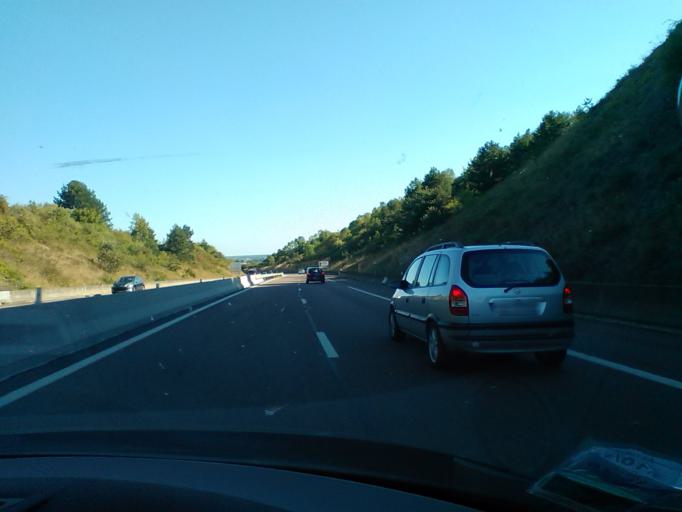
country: FR
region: Bourgogne
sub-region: Departement de la Cote-d'Or
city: Savigny-les-Beaune
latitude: 47.0581
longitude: 4.8148
